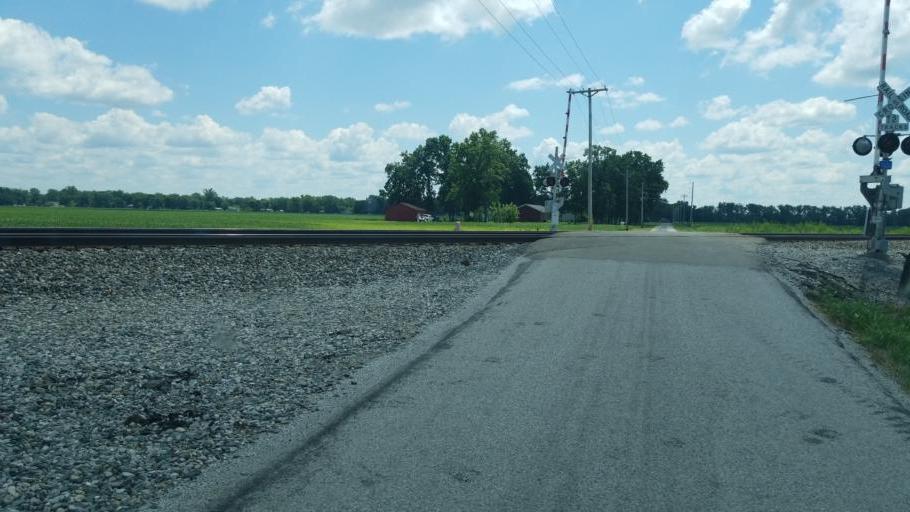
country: US
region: Ohio
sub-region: Marion County
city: Marion
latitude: 40.6593
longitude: -83.0923
